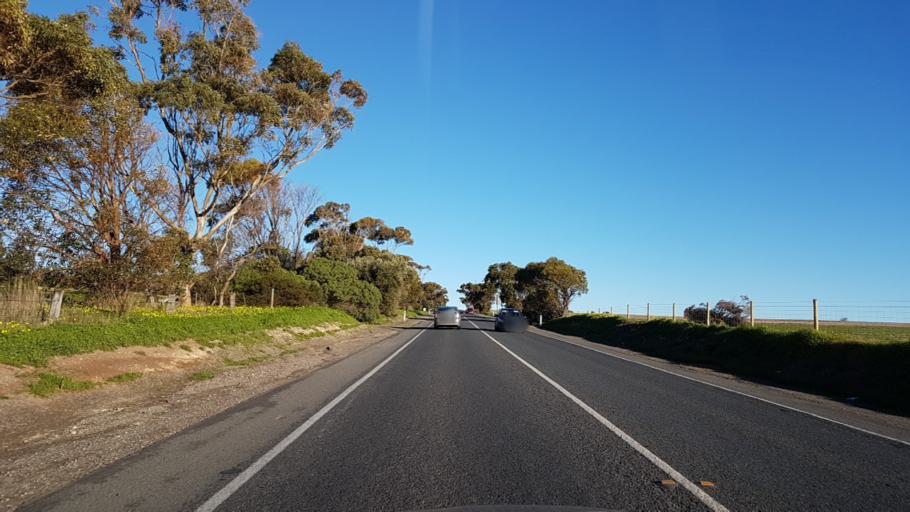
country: AU
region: South Australia
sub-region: Onkaparinga
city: Aldinga
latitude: -35.2447
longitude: 138.4943
